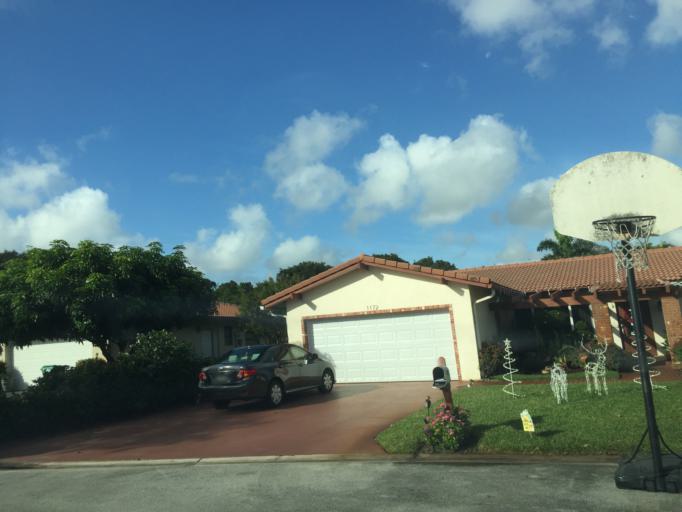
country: US
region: Florida
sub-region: Broward County
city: North Lauderdale
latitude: 26.2453
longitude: -80.2404
